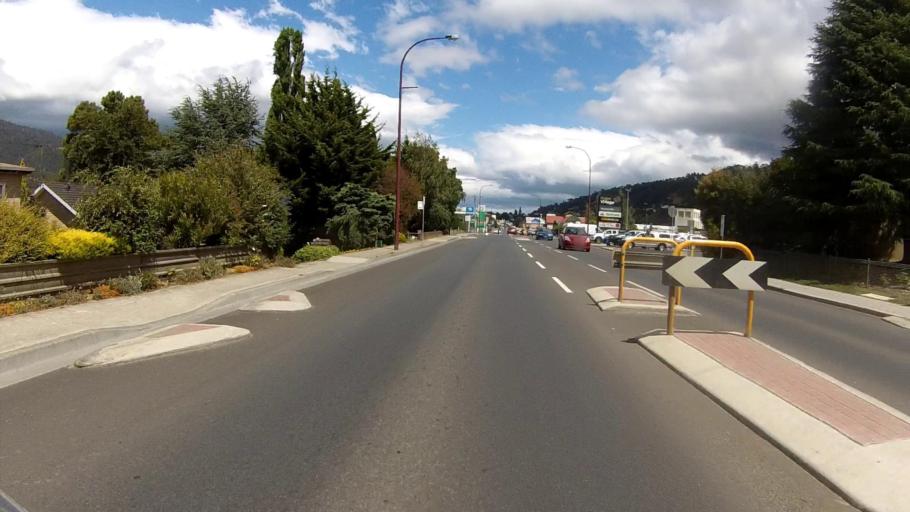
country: AU
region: Tasmania
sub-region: Huon Valley
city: Huonville
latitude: -43.0276
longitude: 147.0502
